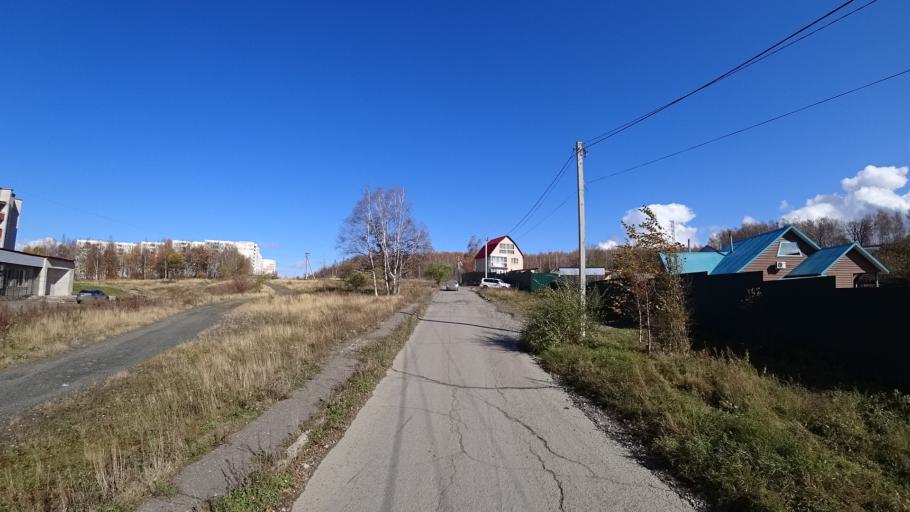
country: RU
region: Khabarovsk Krai
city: Amursk
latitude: 50.2403
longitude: 136.9190
